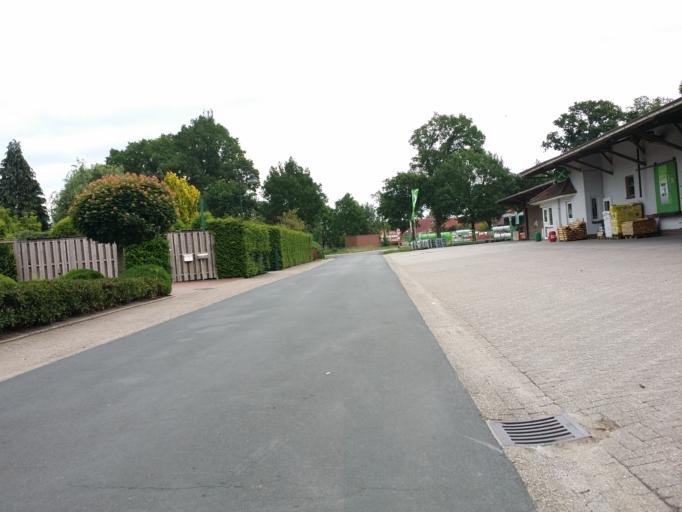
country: DE
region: Lower Saxony
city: Wiefelstede
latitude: 53.3044
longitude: 8.0576
